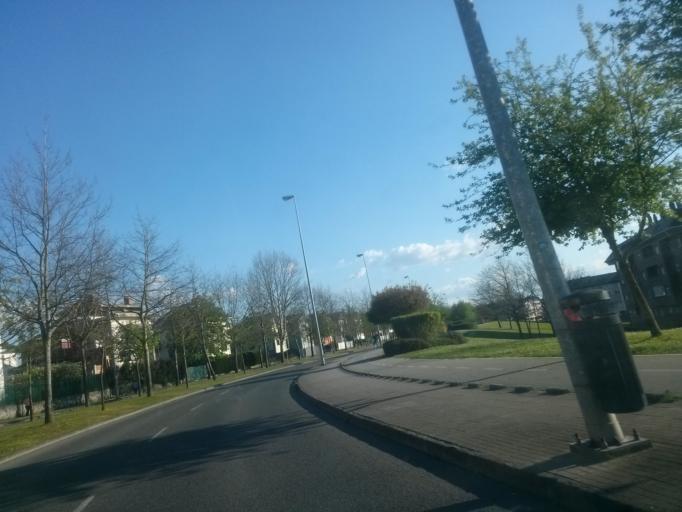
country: ES
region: Galicia
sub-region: Provincia de Lugo
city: Lugo
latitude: 43.0007
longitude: -7.5542
